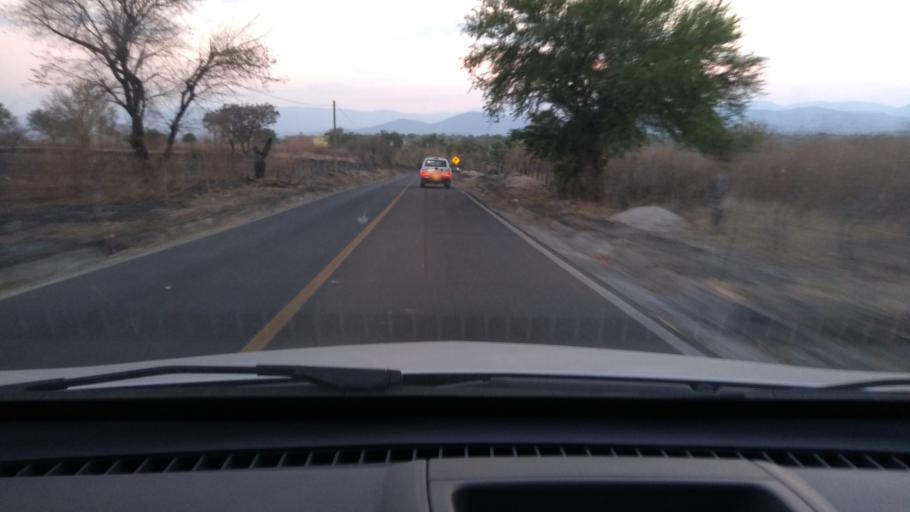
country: MX
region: Morelos
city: Coatetelco
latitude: 18.7227
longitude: -99.3034
